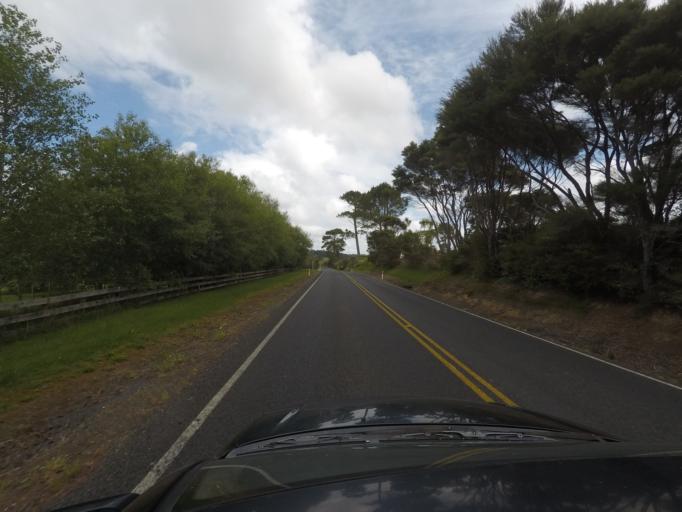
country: NZ
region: Auckland
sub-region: Auckland
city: Parakai
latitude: -36.6520
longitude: 174.5212
